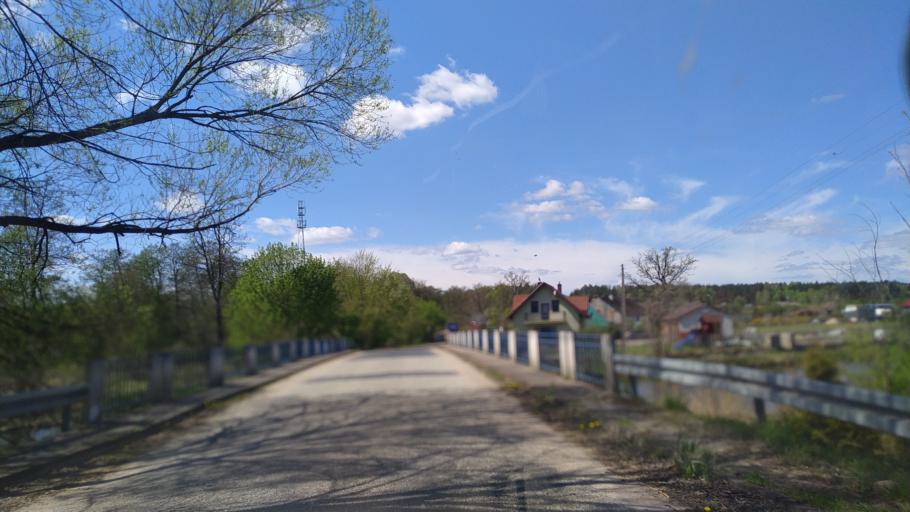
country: PL
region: Greater Poland Voivodeship
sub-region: Powiat zlotowski
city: Tarnowka
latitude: 53.2627
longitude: 16.7804
